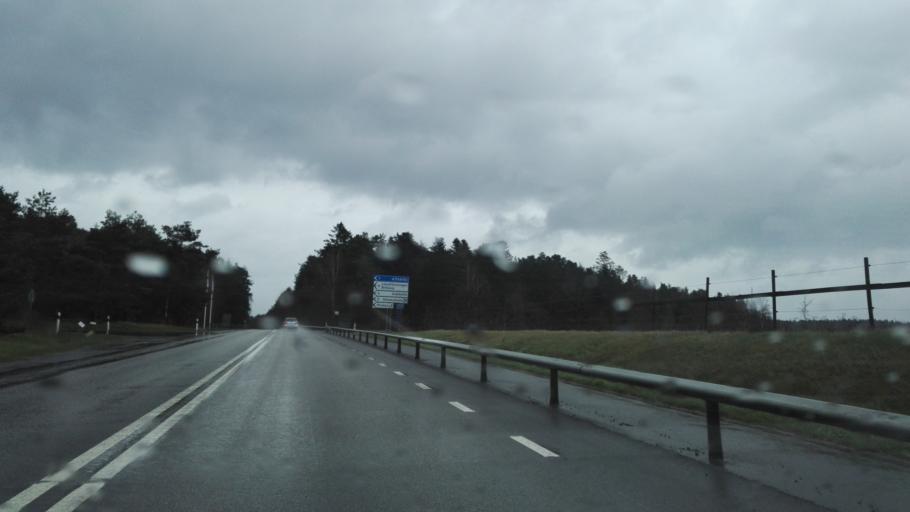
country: SE
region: Skane
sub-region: Kristianstads Kommun
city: Degeberga
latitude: 55.7334
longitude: 14.1117
